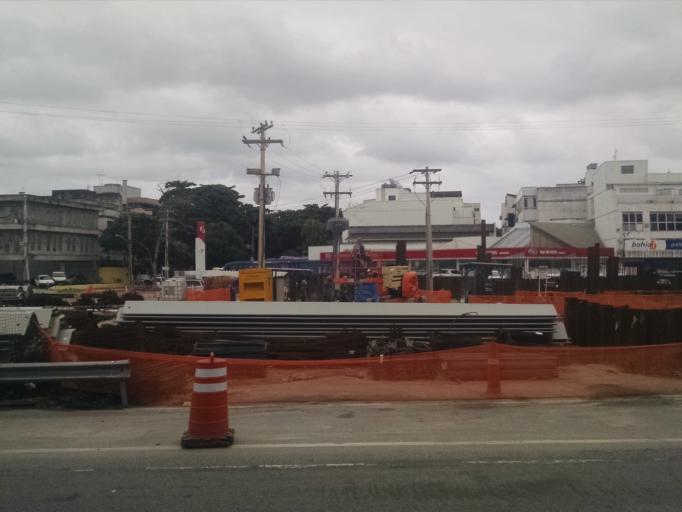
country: BR
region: Rio de Janeiro
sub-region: Rio De Janeiro
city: Rio de Janeiro
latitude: -23.0066
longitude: -43.3094
